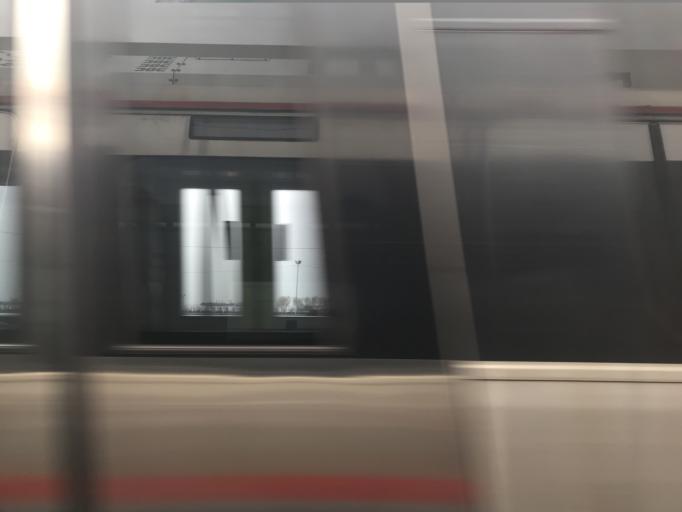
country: TR
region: Istanbul
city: Zeytinburnu
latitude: 40.9927
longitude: 28.9166
